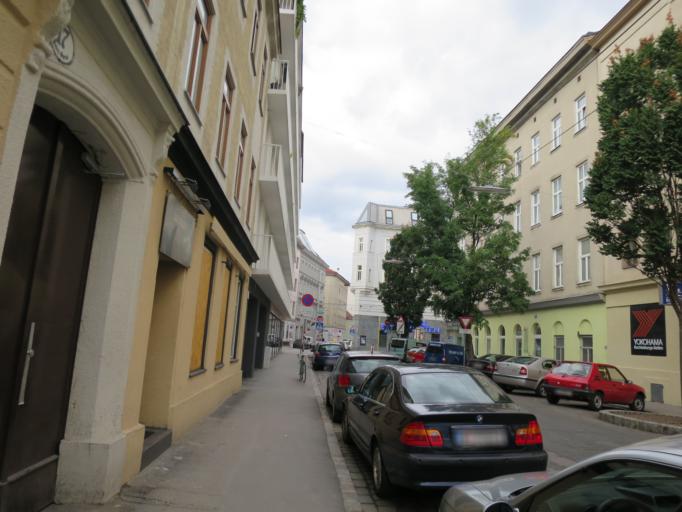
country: AT
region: Vienna
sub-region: Wien Stadt
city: Vienna
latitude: 48.2139
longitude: 16.3332
